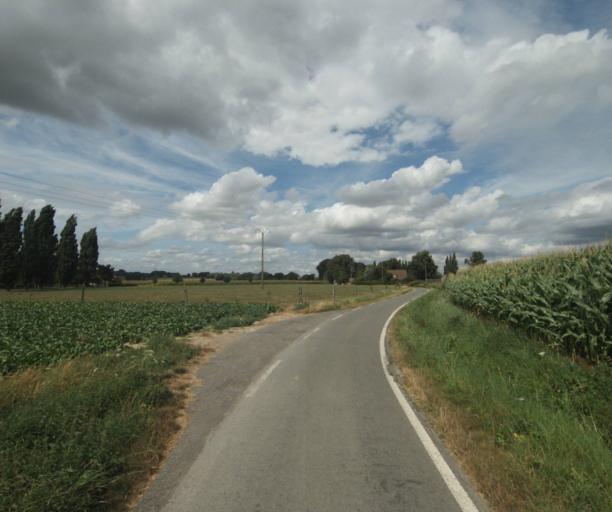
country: FR
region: Nord-Pas-de-Calais
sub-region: Departement du Nord
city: Linselles
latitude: 50.7523
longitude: 3.0703
